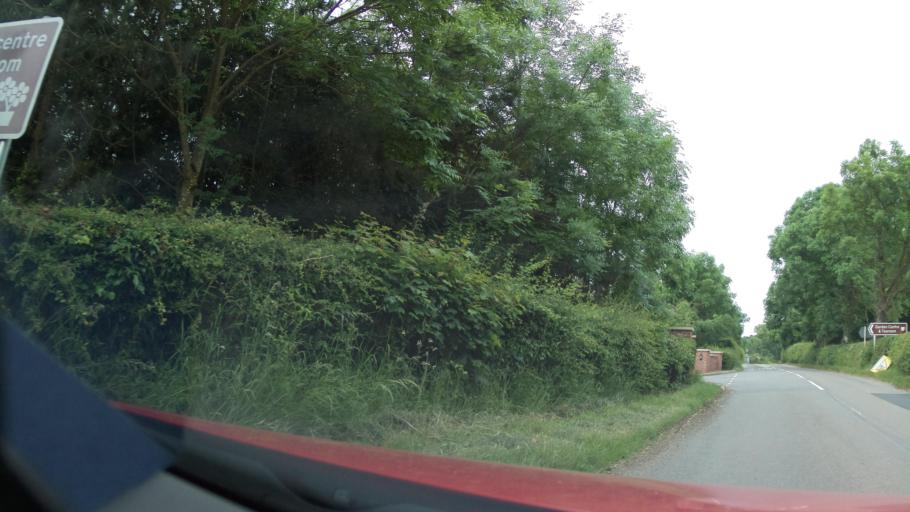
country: GB
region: England
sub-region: District of Rutland
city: Langham
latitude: 52.6812
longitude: -0.7994
